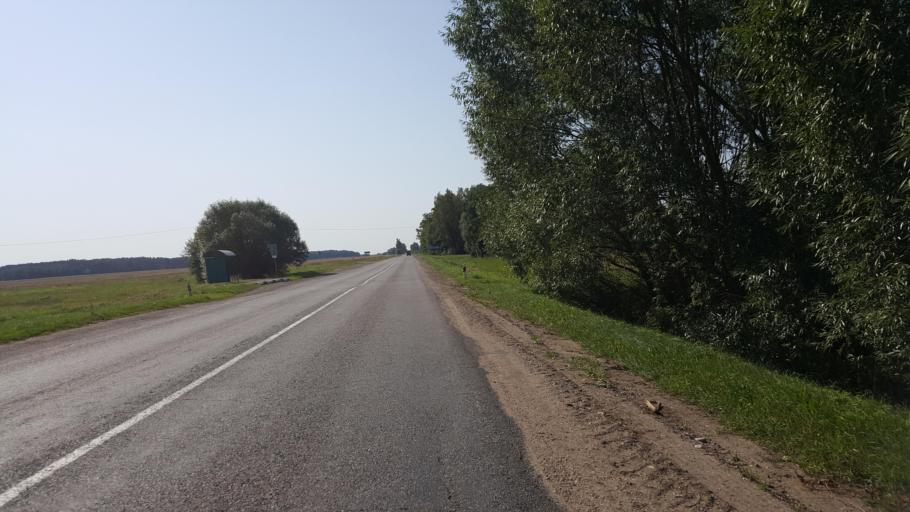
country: BY
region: Brest
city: Zhabinka
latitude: 52.2575
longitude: 23.9649
